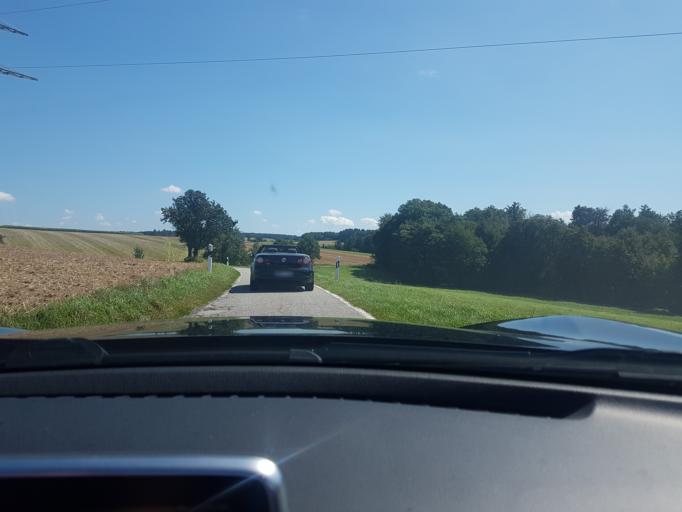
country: DE
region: Baden-Wuerttemberg
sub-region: Karlsruhe Region
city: Reichartshausen
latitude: 49.3915
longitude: 8.9092
